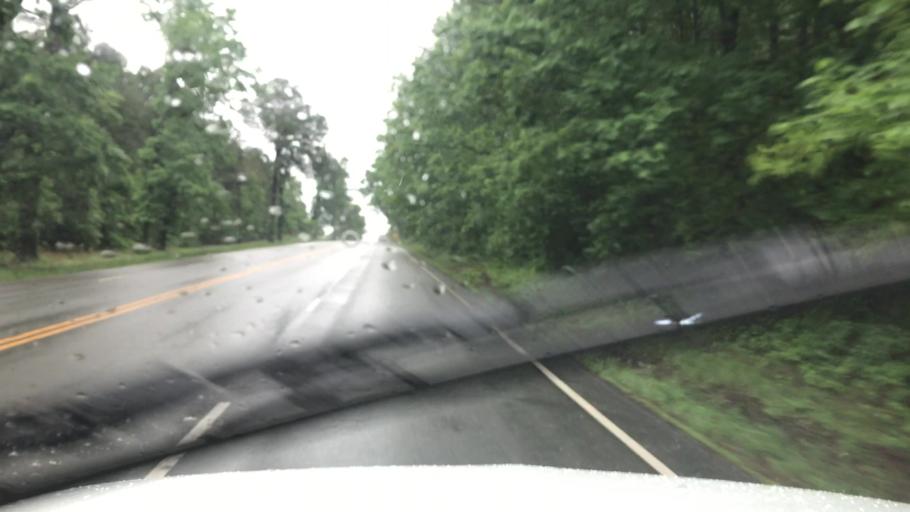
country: US
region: Virginia
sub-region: Hanover County
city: Ashland
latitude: 37.8404
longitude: -77.4665
